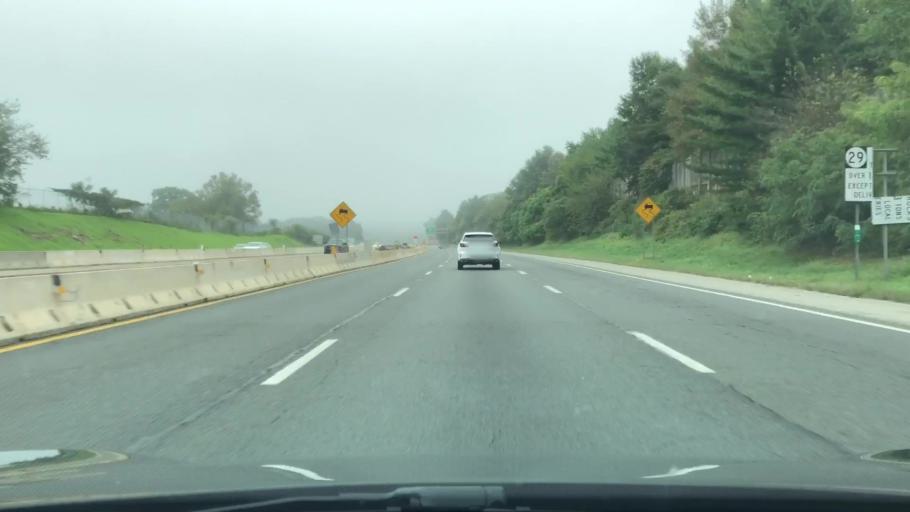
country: US
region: Pennsylvania
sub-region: Bucks County
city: Yardley
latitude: 40.2686
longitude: -74.8377
